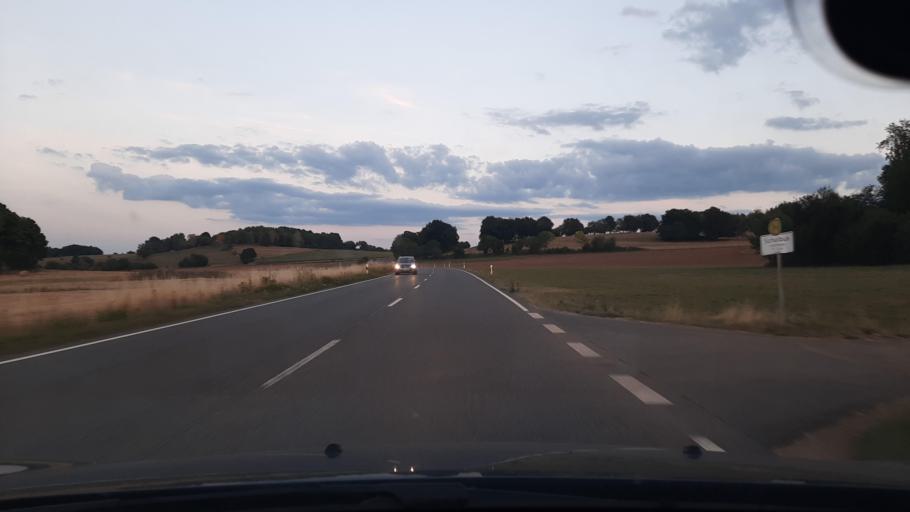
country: DE
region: North Rhine-Westphalia
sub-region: Regierungsbezirk Koln
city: Nettersheim
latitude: 50.5181
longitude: 6.6404
